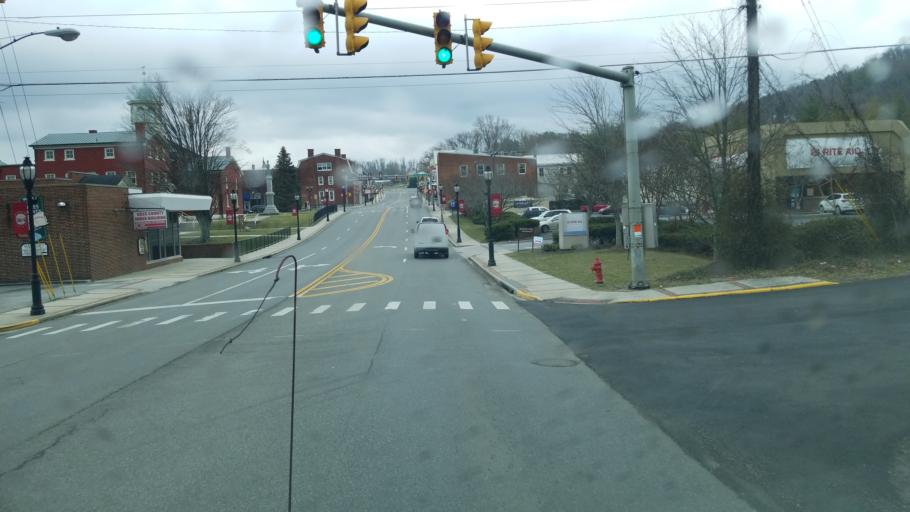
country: US
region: Virginia
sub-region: Giles County
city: Pearisburg
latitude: 37.3277
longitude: -80.7358
